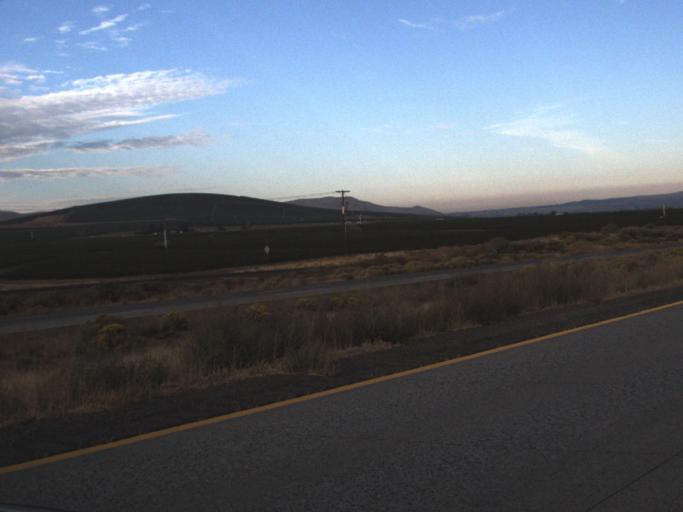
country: US
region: Washington
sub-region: Benton County
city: West Richland
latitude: 46.2533
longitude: -119.3755
